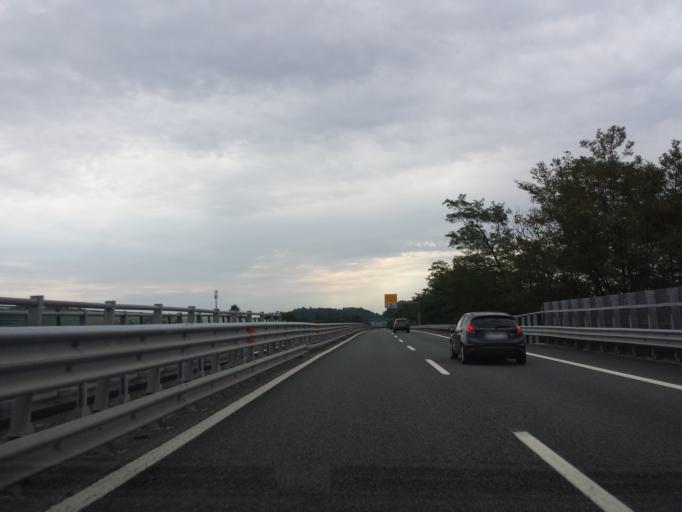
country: IT
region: Lombardy
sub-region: Provincia di Varese
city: Besnate
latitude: 45.6922
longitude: 8.7628
